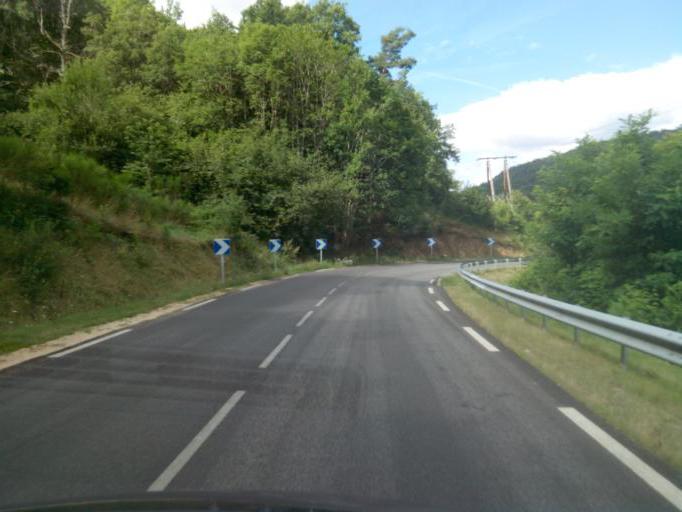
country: FR
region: Auvergne
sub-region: Departement de la Haute-Loire
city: Vorey
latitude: 45.2026
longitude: 3.9350
